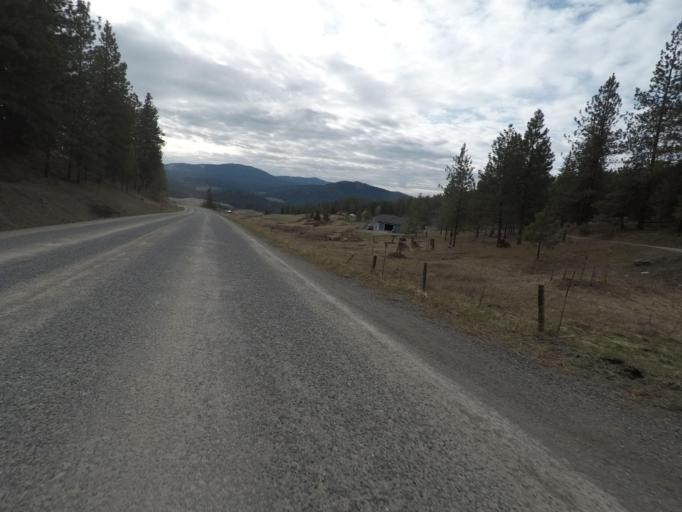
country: US
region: Washington
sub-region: Stevens County
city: Colville
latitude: 48.5026
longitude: -117.8508
